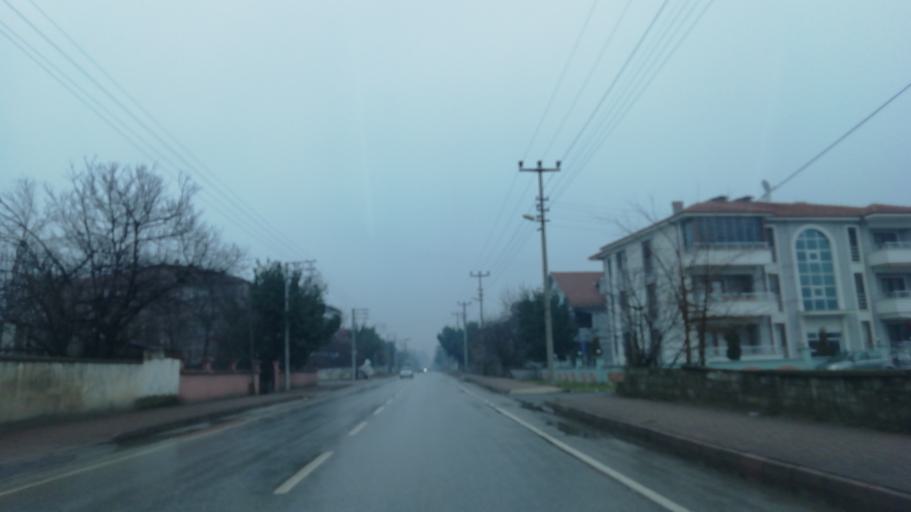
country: TR
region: Sakarya
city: Akyazi
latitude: 40.6635
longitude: 30.6196
